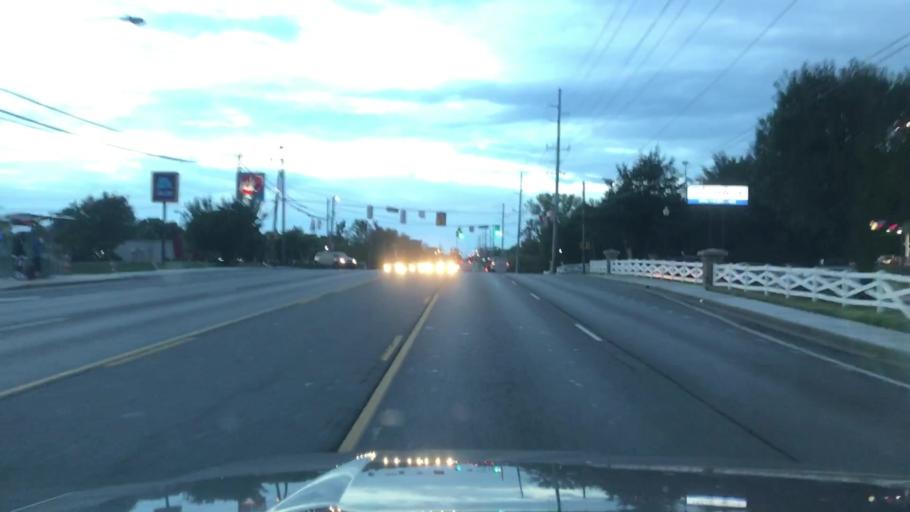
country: US
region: Tennessee
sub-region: Rutherford County
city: La Vergne
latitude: 36.0883
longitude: -86.6495
